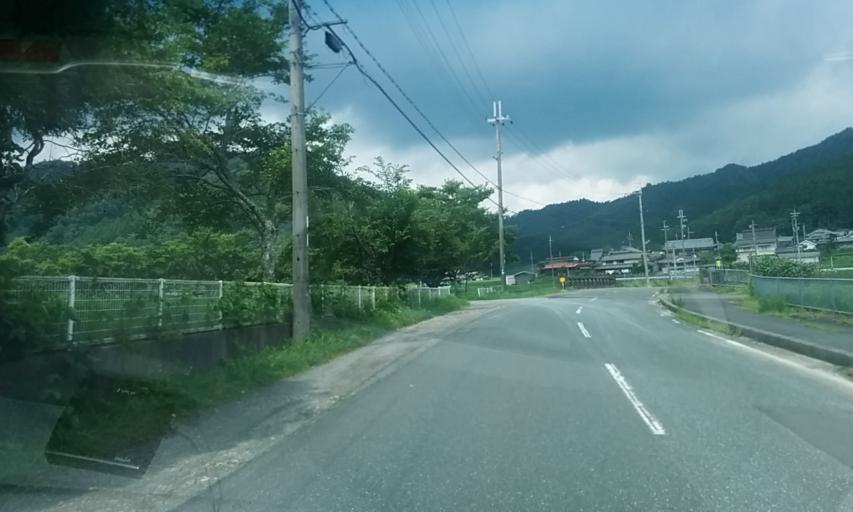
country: JP
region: Kyoto
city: Kameoka
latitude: 35.1406
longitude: 135.4209
